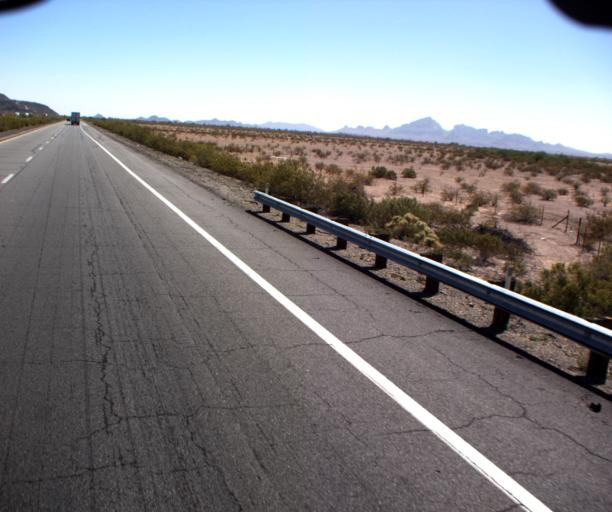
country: US
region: Arizona
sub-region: La Paz County
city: Salome
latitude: 33.5354
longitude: -113.1469
